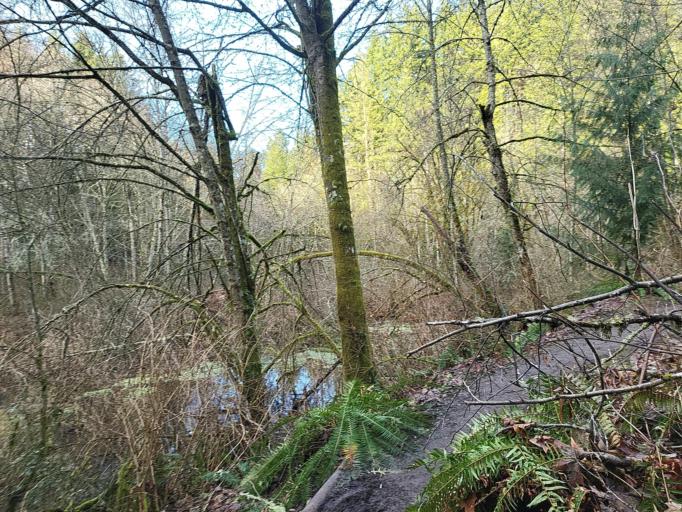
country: US
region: Washington
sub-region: King County
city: Newcastle
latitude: 47.5432
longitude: -122.1495
